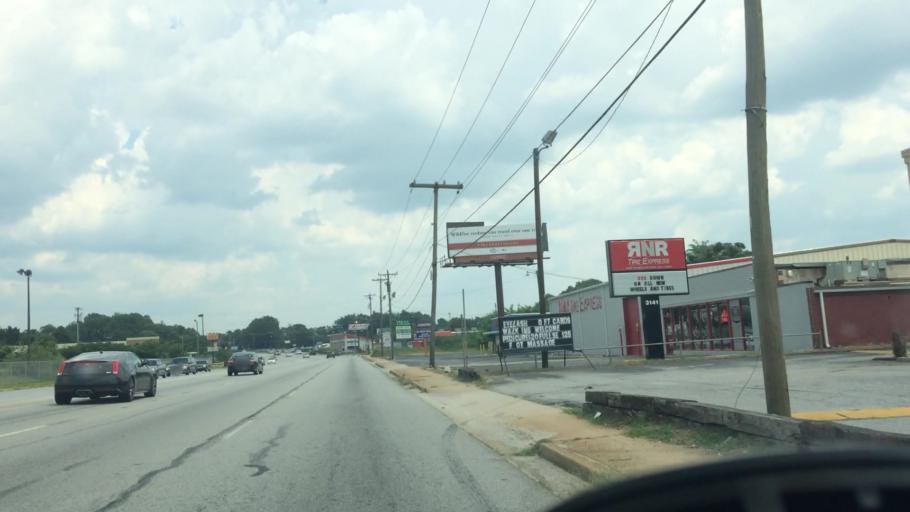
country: US
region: South Carolina
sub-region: Greenville County
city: Sans Souci
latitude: 34.8887
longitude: -82.3988
